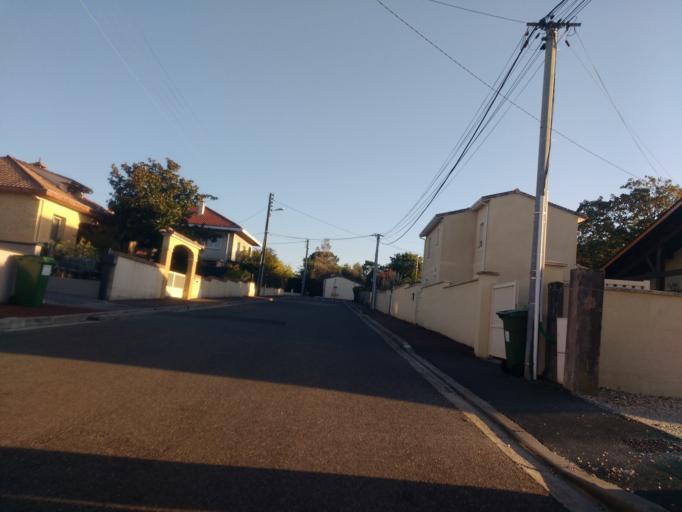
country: FR
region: Aquitaine
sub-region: Departement de la Gironde
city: Pessac
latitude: 44.8116
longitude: -0.6384
